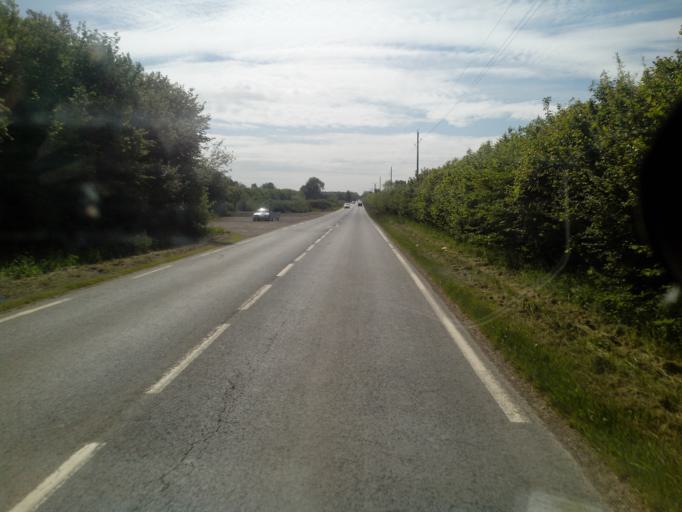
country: FR
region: Lower Normandy
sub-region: Departement du Calvados
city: Touques
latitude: 49.2632
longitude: 0.1339
